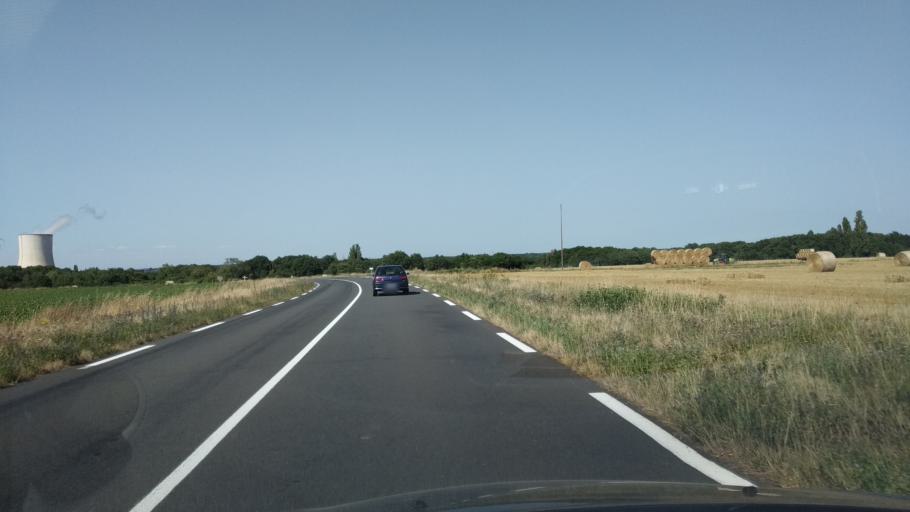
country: FR
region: Poitou-Charentes
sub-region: Departement de la Vienne
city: Lussac-les-Chateaux
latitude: 46.4325
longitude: 0.6474
